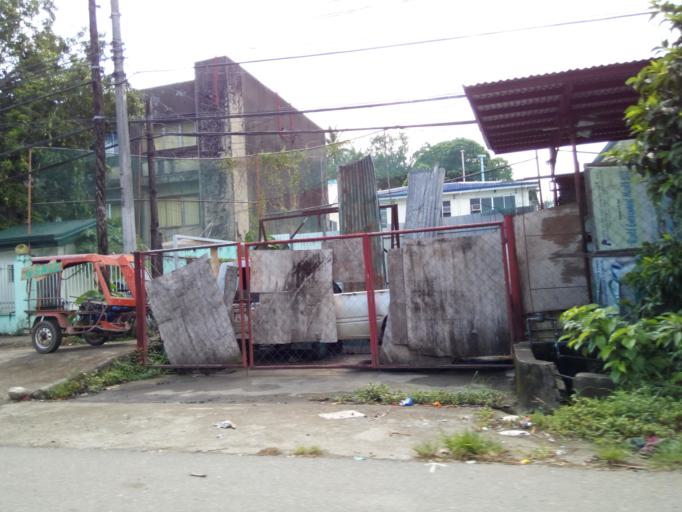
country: PH
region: Caraga
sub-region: Province of Surigao del Norte
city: Surigao
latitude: 9.7785
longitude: 125.4827
